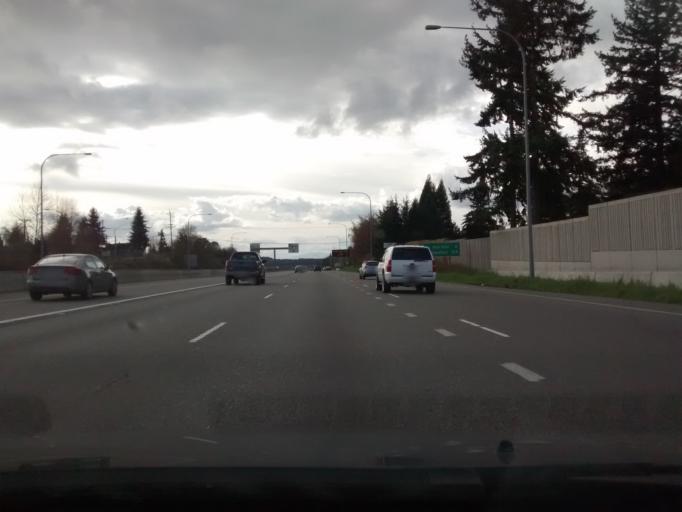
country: US
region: Washington
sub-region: Pierce County
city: Fircrest
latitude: 47.2584
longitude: -122.5230
